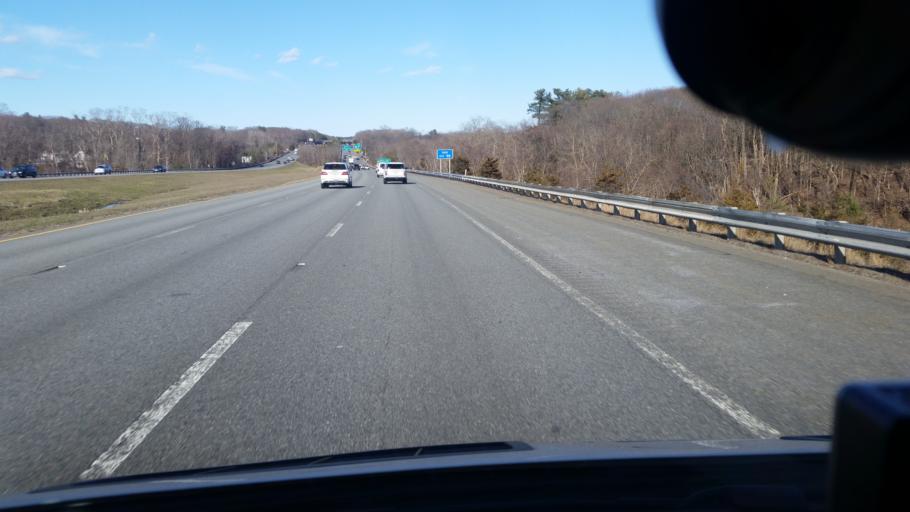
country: US
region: Massachusetts
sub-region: Essex County
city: Amesbury
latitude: 42.8429
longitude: -70.9254
